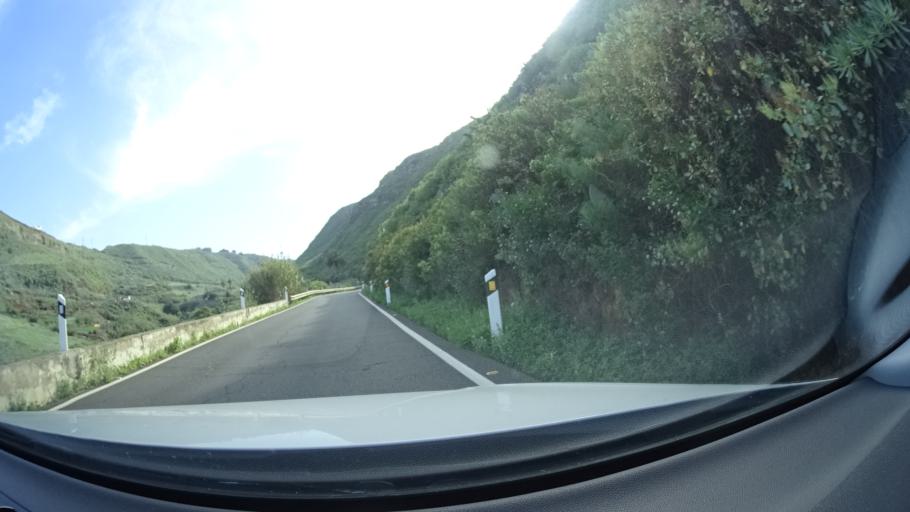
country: ES
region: Canary Islands
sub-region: Provincia de Las Palmas
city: Guia
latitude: 28.1115
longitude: -15.6414
